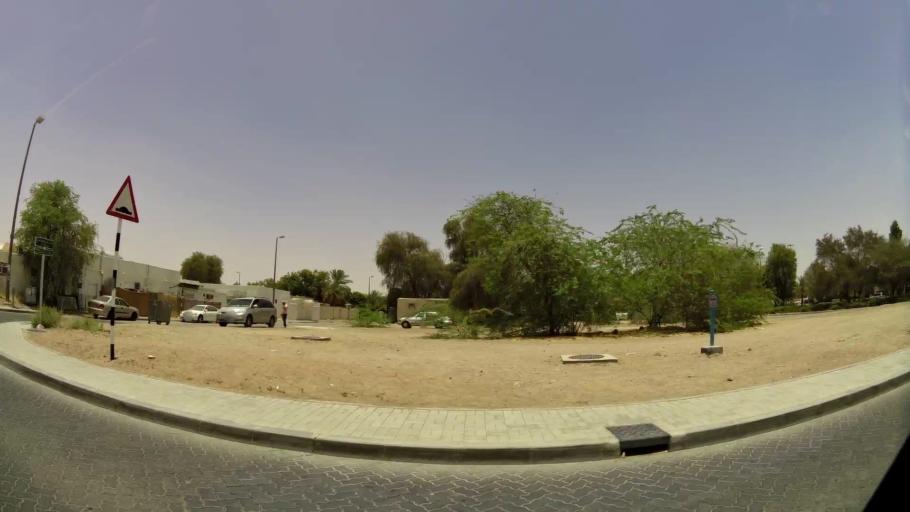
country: OM
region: Al Buraimi
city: Al Buraymi
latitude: 24.2635
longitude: 55.7395
